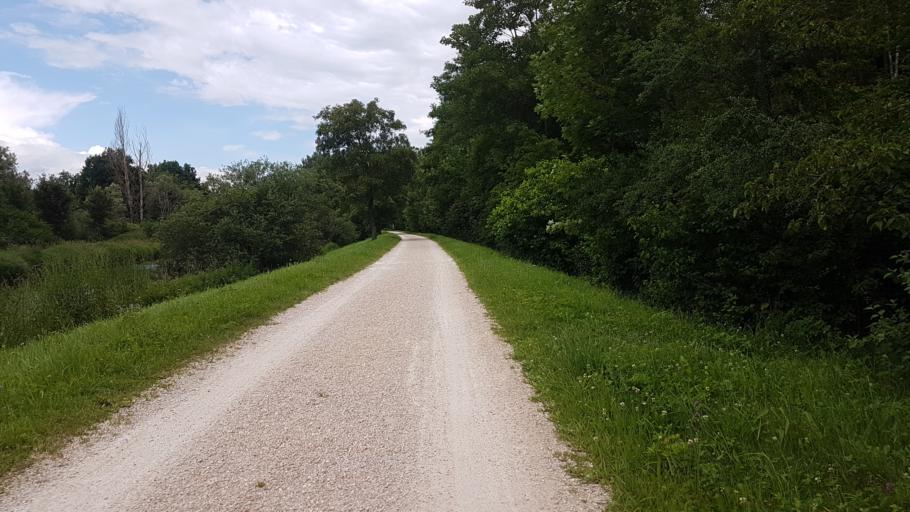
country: DE
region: Baden-Wuerttemberg
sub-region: Tuebingen Region
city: Neufra
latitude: 48.1410
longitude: 9.4733
